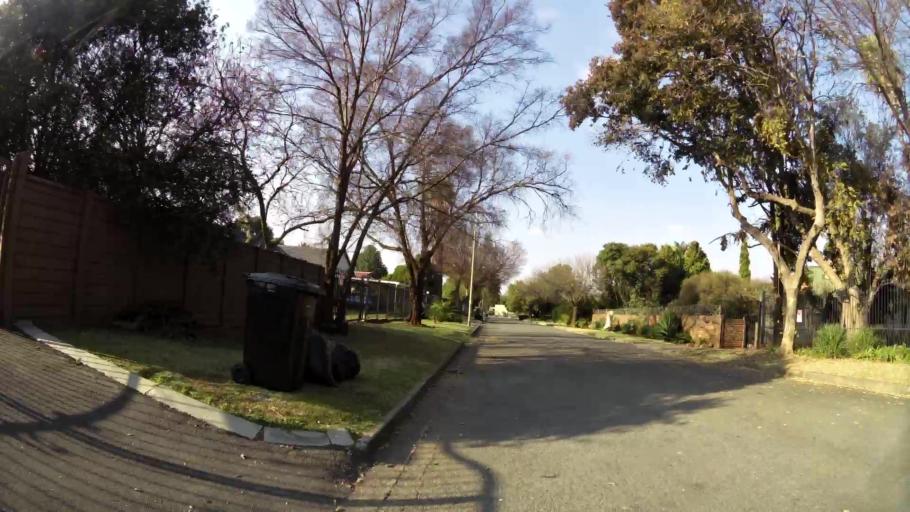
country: ZA
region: Gauteng
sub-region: City of Johannesburg Metropolitan Municipality
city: Modderfontein
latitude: -26.0790
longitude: 28.2084
